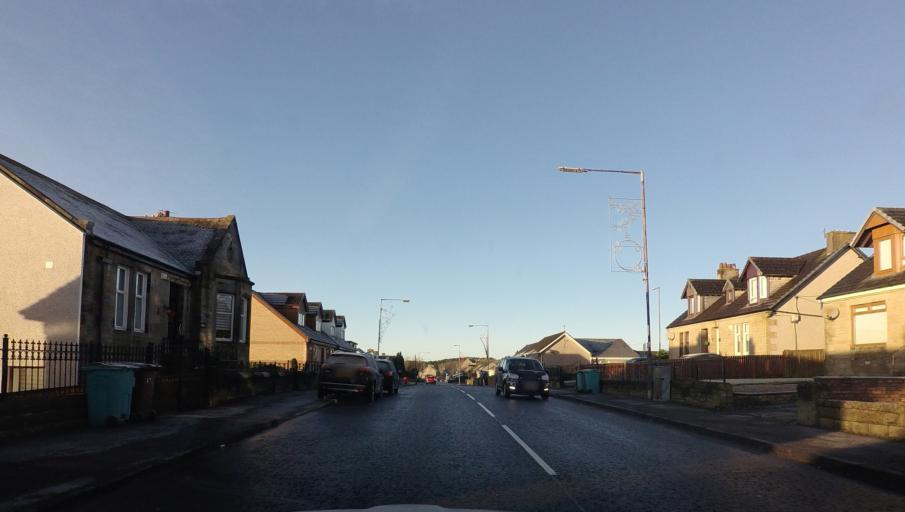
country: GB
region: Scotland
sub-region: North Lanarkshire
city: Shotts
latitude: 55.8193
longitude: -3.8018
